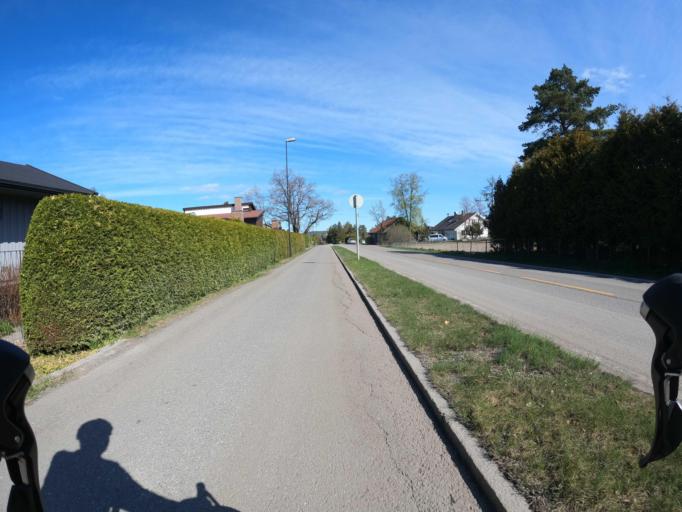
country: NO
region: Akershus
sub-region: Skedsmo
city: Lillestrom
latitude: 59.9642
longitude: 11.0087
